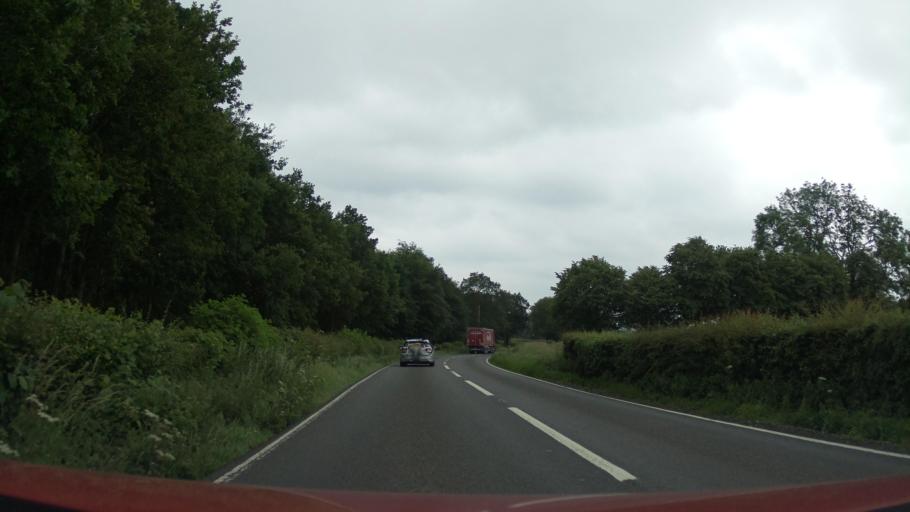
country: GB
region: England
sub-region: Derbyshire
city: Rodsley
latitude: 52.9073
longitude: -1.7648
